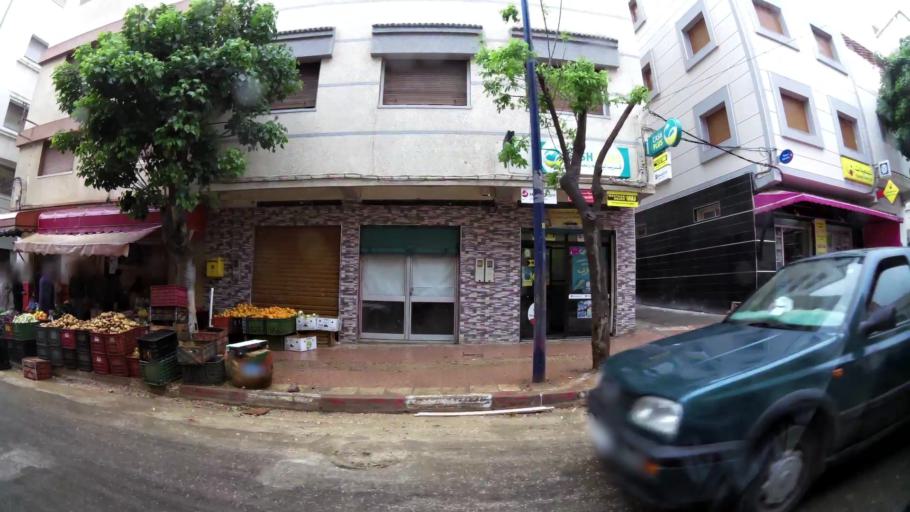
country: MA
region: Taza-Al Hoceima-Taounate
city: Al Hoceima
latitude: 35.2513
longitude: -3.9344
